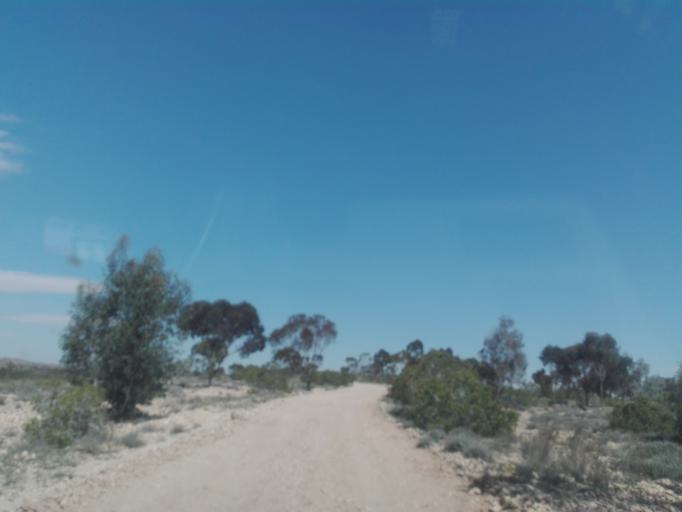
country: TN
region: Safaqis
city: Sfax
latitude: 34.7006
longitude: 10.5301
